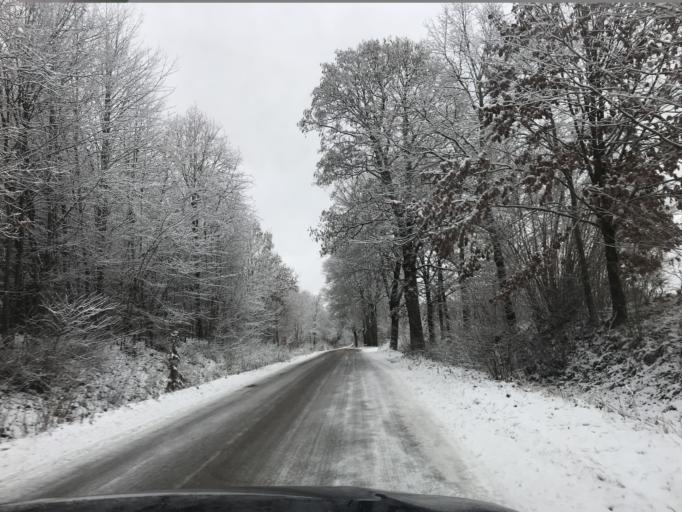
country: PL
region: Pomeranian Voivodeship
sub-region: Powiat bytowski
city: Parchowo
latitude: 54.2367
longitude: 17.5756
